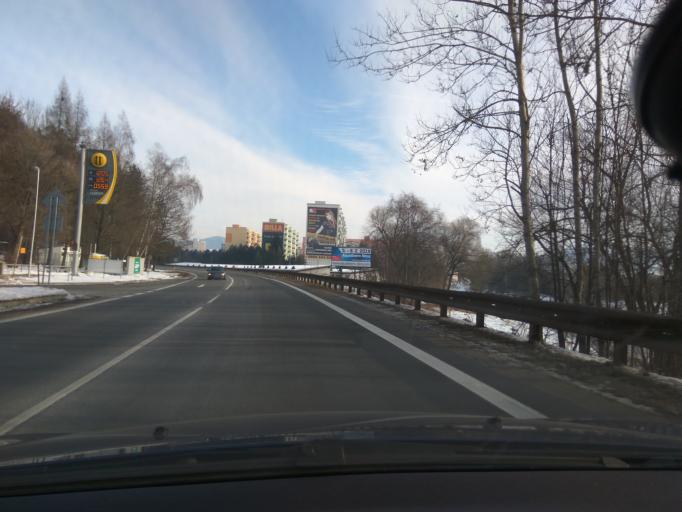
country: SK
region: Banskobystricky
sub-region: Okres Banska Bystrica
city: Brezno
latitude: 48.8058
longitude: 19.6205
